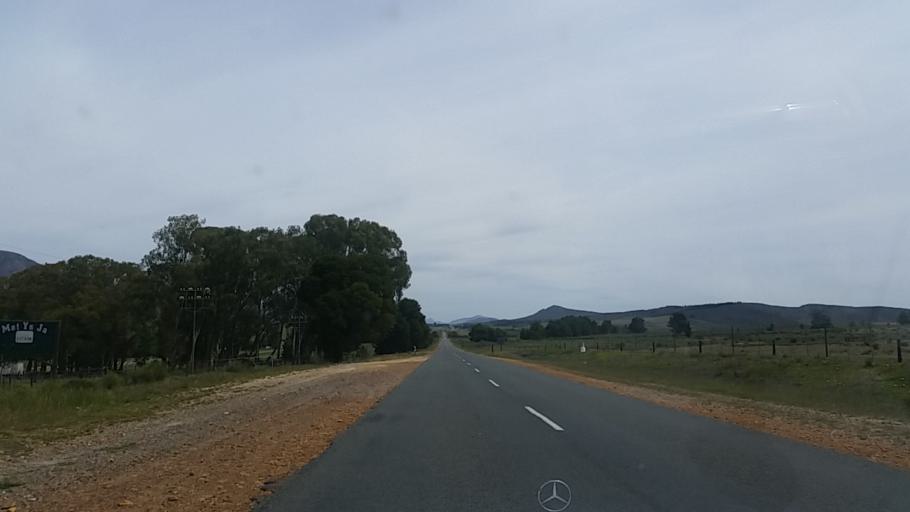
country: ZA
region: Western Cape
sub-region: Eden District Municipality
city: Knysna
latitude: -33.7615
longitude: 22.8501
